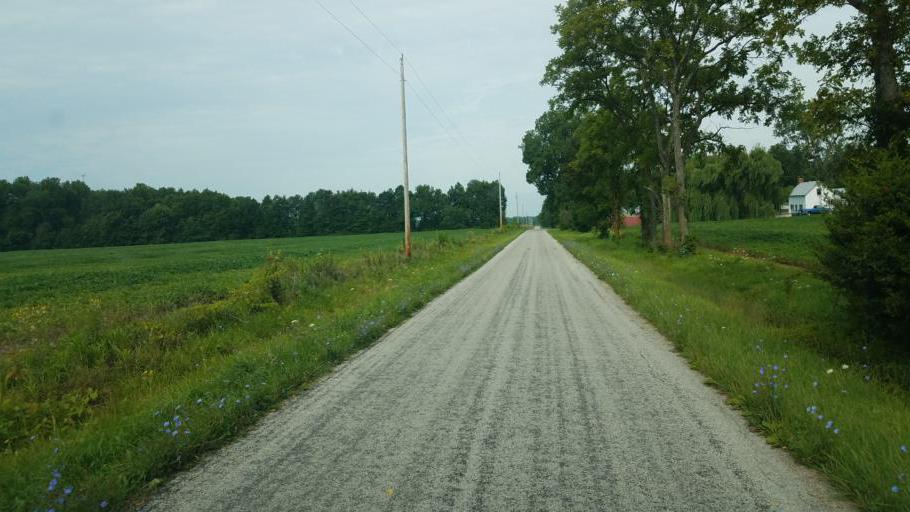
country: US
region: Ohio
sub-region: Morrow County
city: Cardington
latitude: 40.4778
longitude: -82.9169
